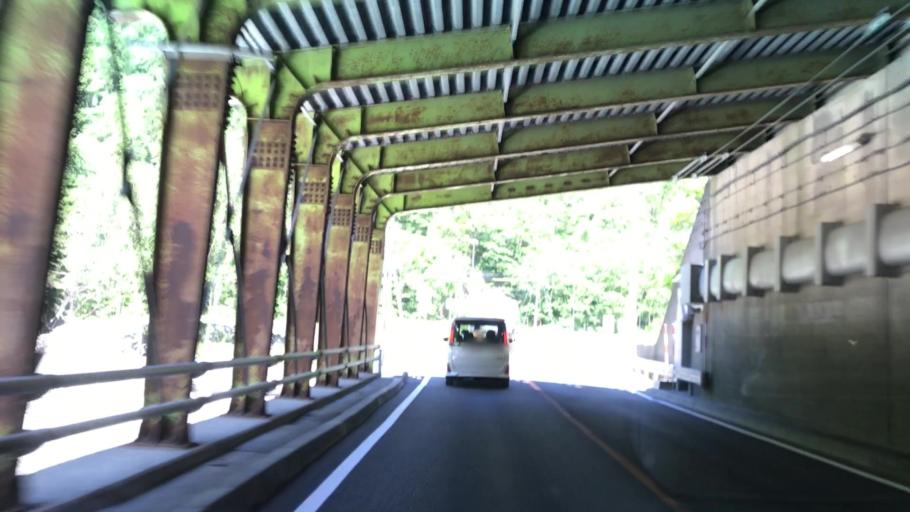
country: JP
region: Hokkaido
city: Shimo-furano
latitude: 42.9443
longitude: 142.5984
